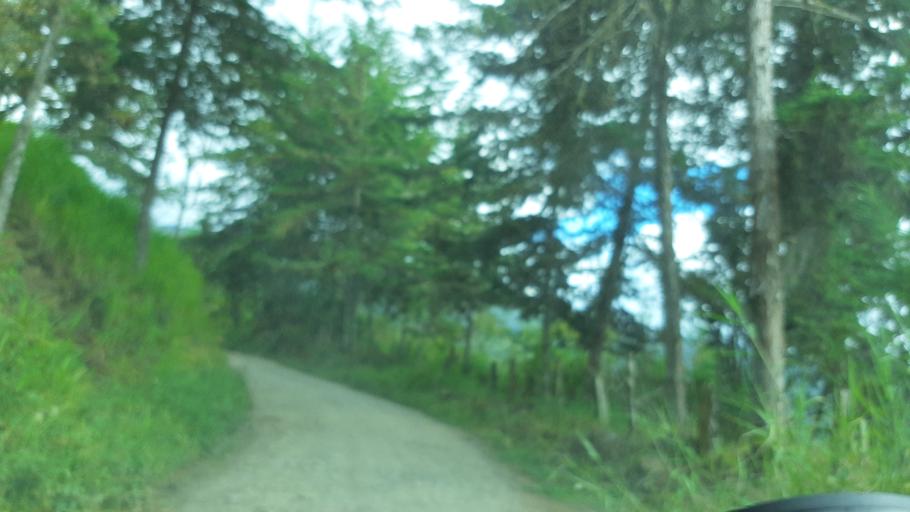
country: CO
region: Boyaca
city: Garagoa
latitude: 5.0408
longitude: -73.3410
